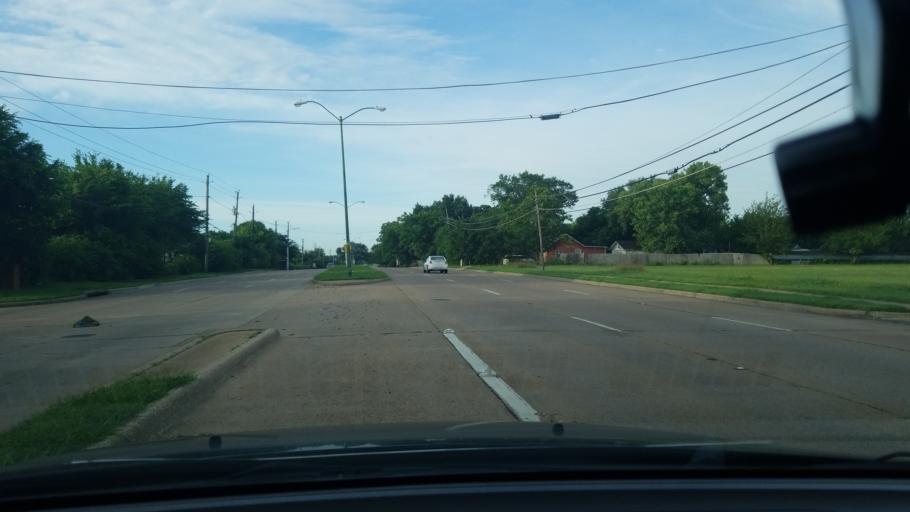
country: US
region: Texas
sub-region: Dallas County
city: Balch Springs
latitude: 32.7602
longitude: -96.6482
